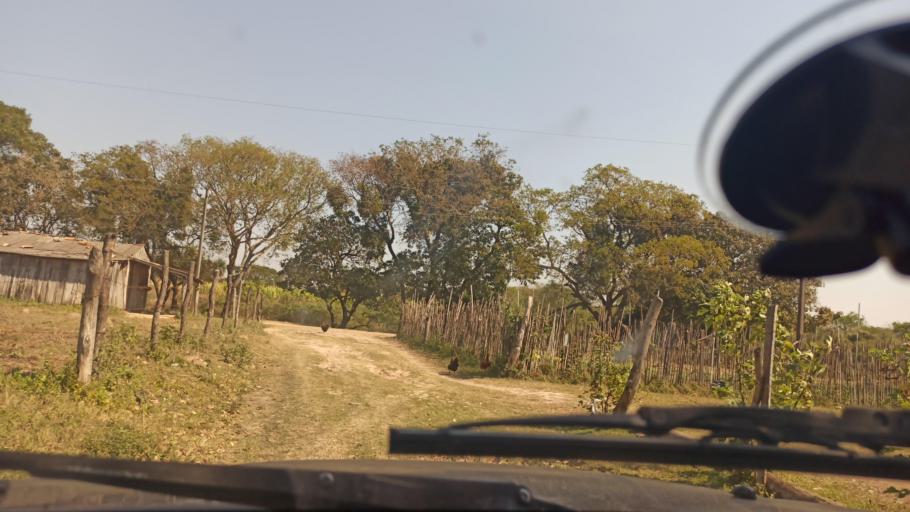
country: PY
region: Asuncion
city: Asuncion
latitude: -25.3307
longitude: -57.6843
